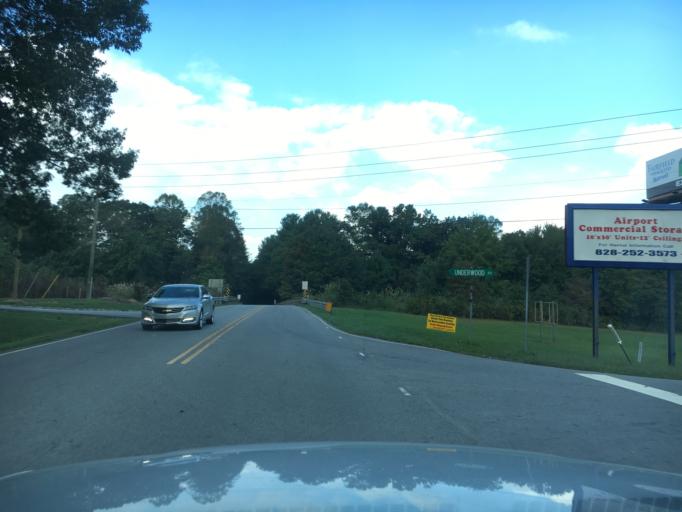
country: US
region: North Carolina
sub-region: Henderson County
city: Fletcher
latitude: 35.4324
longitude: -82.5294
